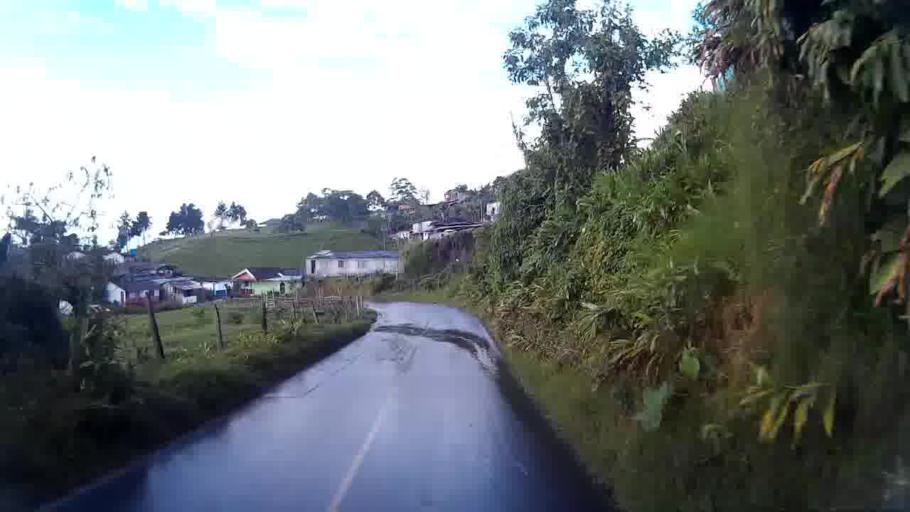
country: CO
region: Quindio
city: Filandia
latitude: 4.6782
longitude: -75.6585
